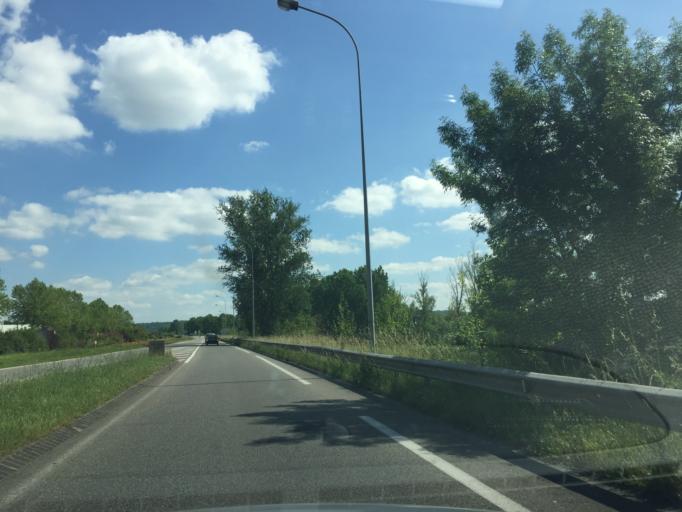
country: FR
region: Aquitaine
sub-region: Departement du Lot-et-Garonne
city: Le Passage
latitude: 44.1824
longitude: 0.6144
